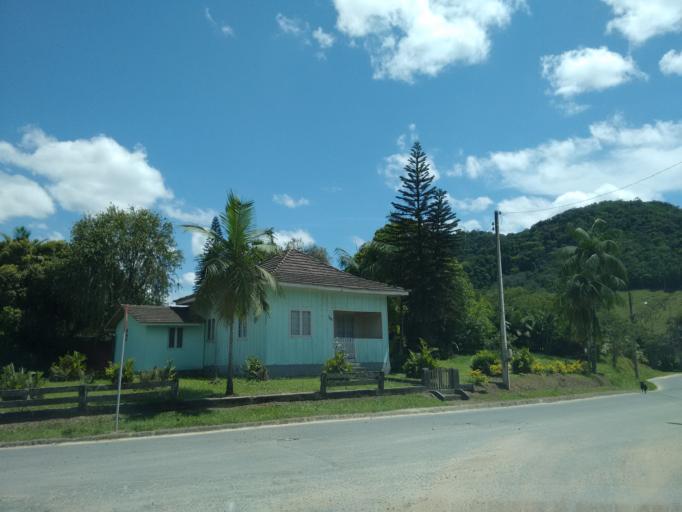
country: BR
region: Santa Catarina
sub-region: Pomerode
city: Pomerode
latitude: -26.7791
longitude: -49.1654
